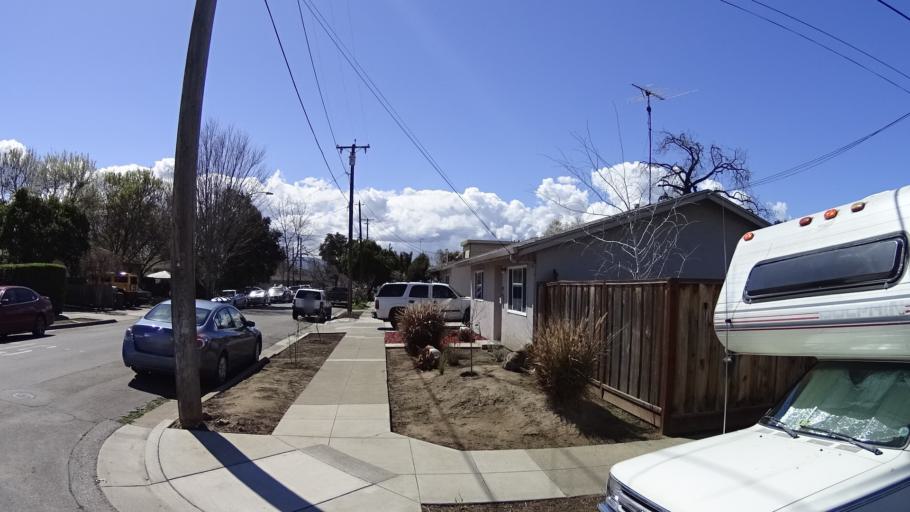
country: US
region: California
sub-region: Santa Clara County
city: San Jose
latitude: 37.3596
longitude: -121.8874
